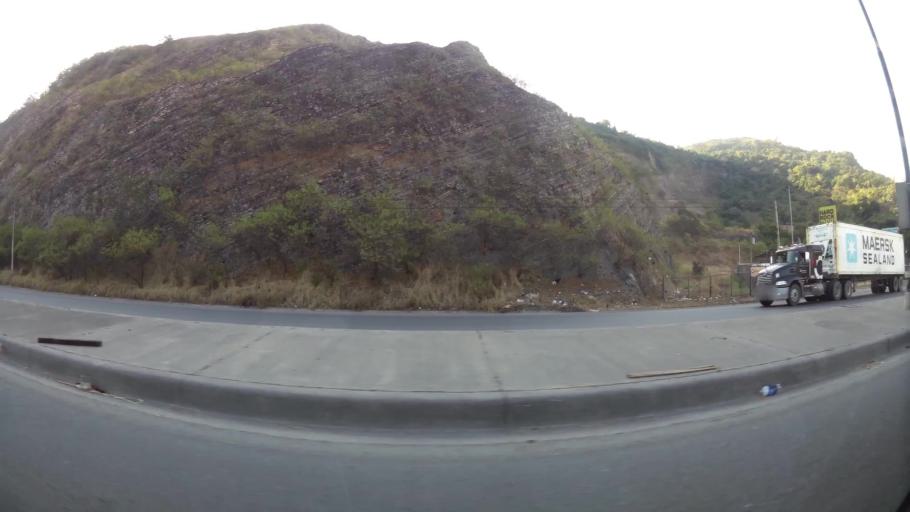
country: EC
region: Guayas
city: Guayaquil
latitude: -2.1834
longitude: -79.9487
